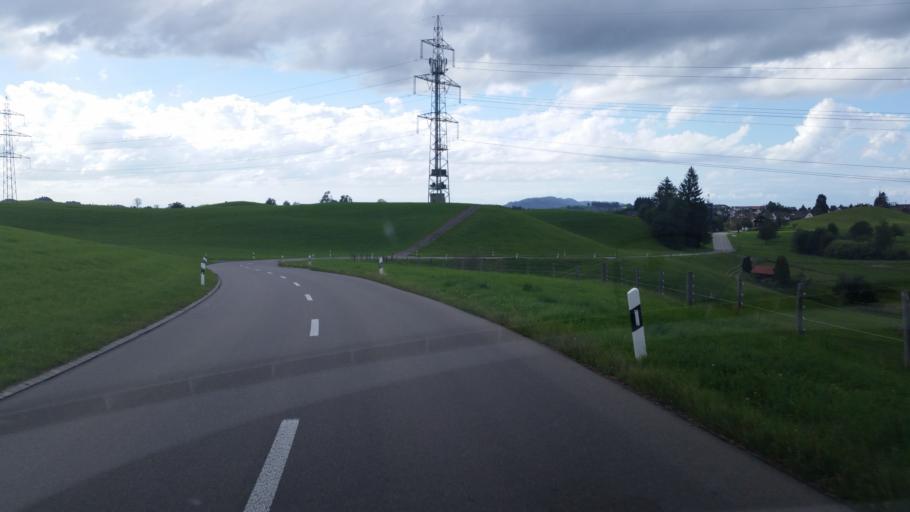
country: CH
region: Zurich
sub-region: Bezirk Horgen
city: Waedenswil / Eichweid
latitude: 47.1849
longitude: 8.6508
